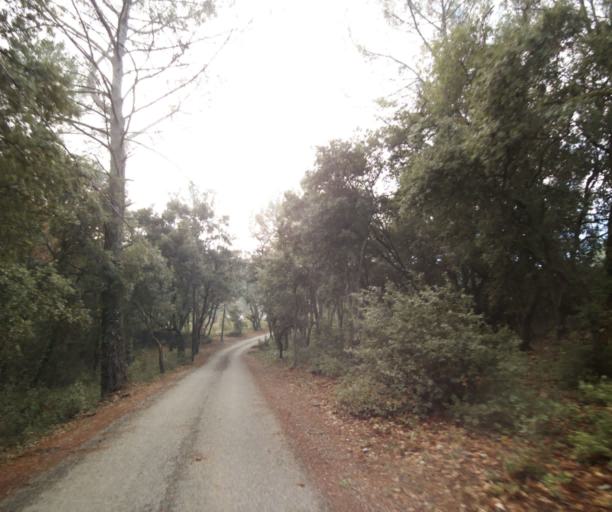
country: FR
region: Provence-Alpes-Cote d'Azur
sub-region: Departement du Var
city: Trans-en-Provence
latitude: 43.4885
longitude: 6.5004
